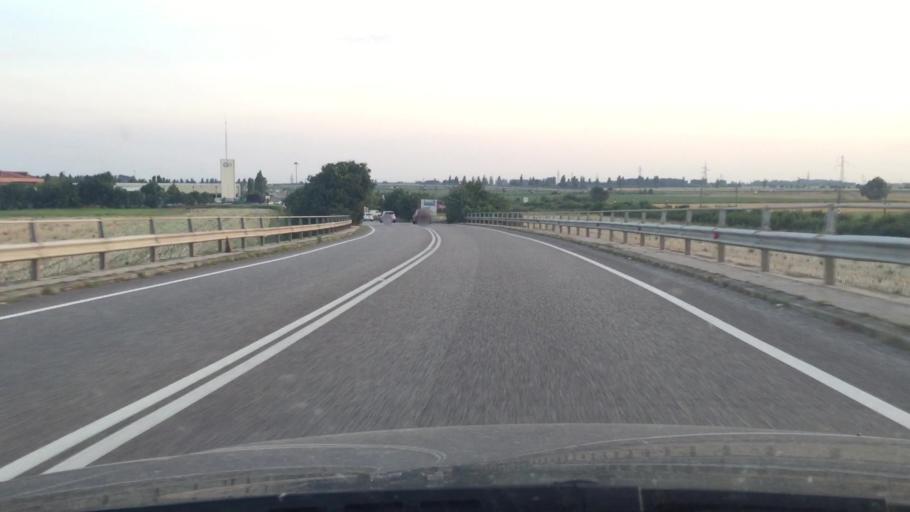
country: IT
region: Emilia-Romagna
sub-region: Provincia di Ferrara
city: Ferrara
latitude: 44.8306
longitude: 11.5953
